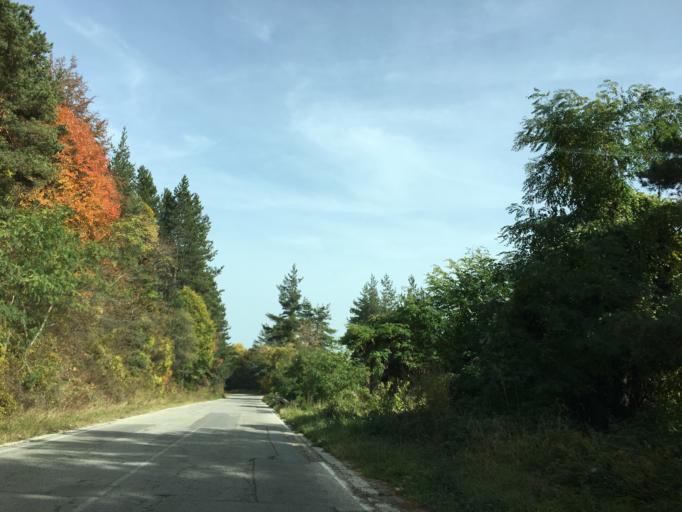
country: BG
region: Sofiya
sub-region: Obshtina Samokov
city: Samokov
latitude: 42.2798
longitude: 23.6399
